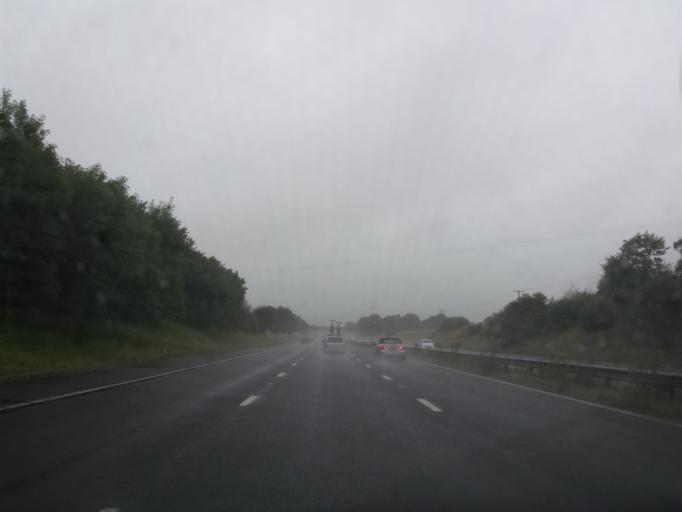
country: GB
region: England
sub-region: Leicestershire
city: Croft
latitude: 52.5771
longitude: -1.2565
